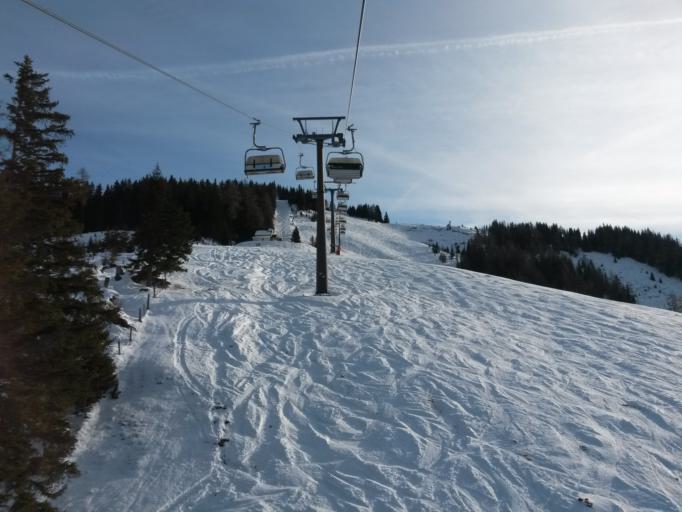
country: AT
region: Salzburg
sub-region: Politischer Bezirk Sankt Johann im Pongau
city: Dorfgastein
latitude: 47.2389
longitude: 13.1308
